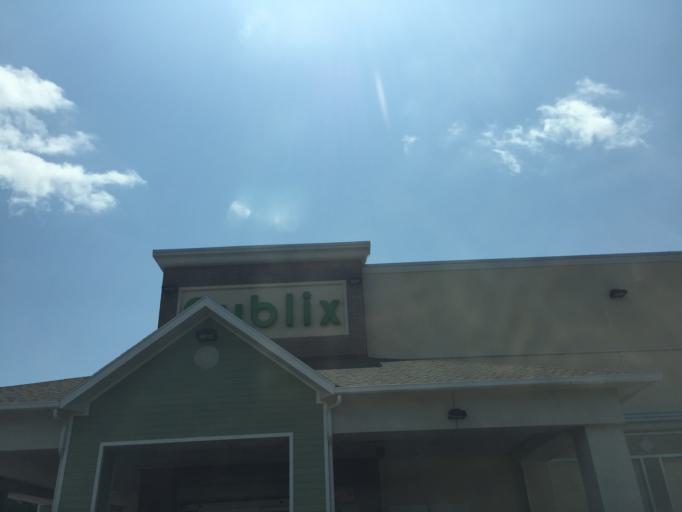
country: US
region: Georgia
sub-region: Chatham County
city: Skidaway Island
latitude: 31.9406
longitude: -81.0506
